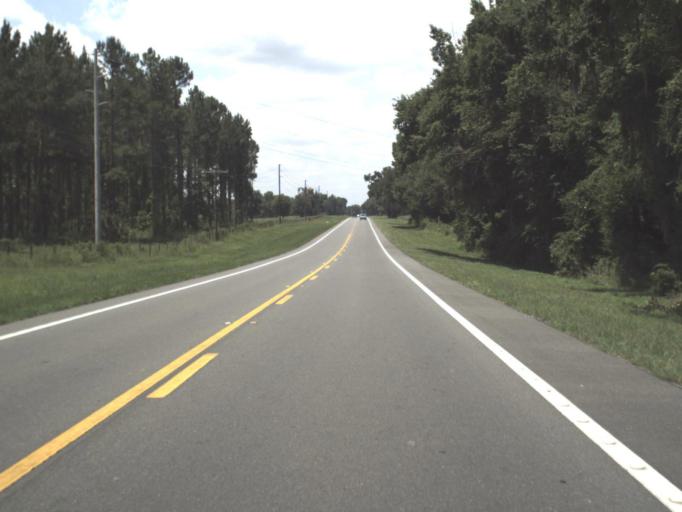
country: US
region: Florida
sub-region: Alachua County
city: Archer
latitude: 29.5047
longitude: -82.4065
